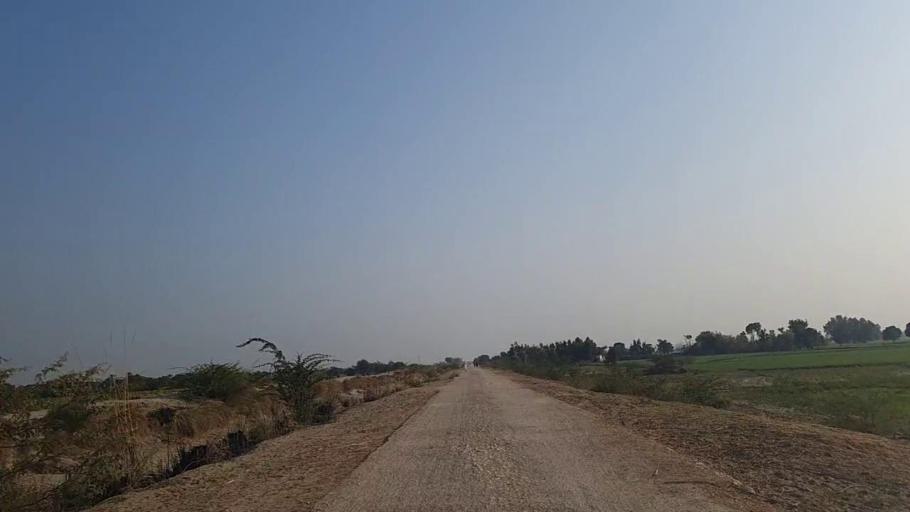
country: PK
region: Sindh
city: Jam Sahib
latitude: 26.2334
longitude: 68.5940
